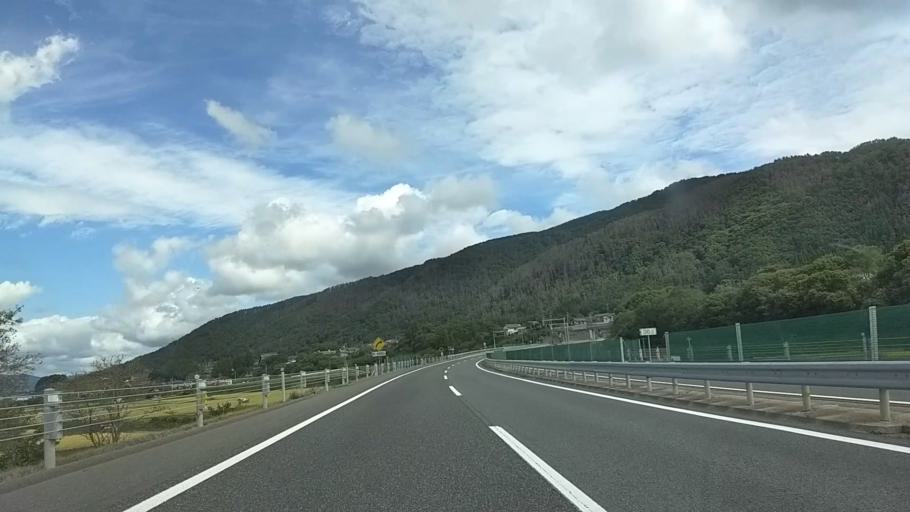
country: JP
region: Nagano
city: Toyoshina
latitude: 36.3250
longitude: 137.9237
